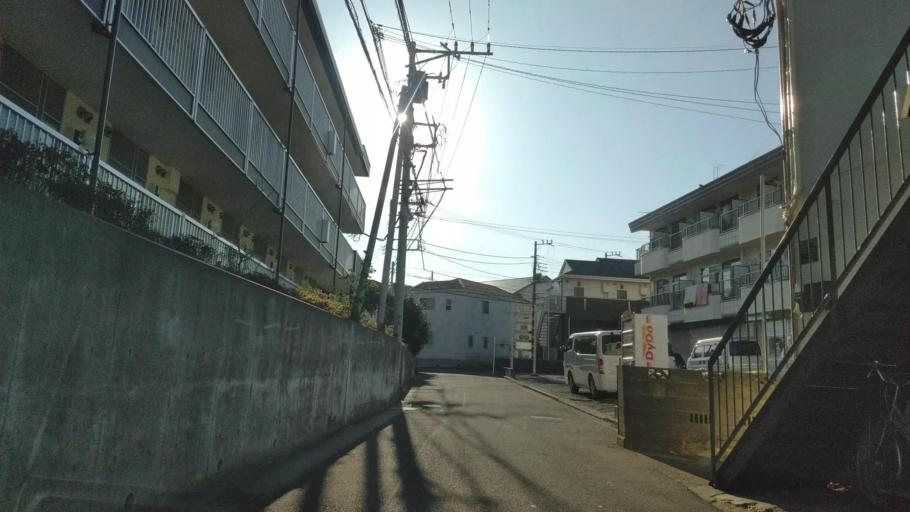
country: JP
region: Kanagawa
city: Hadano
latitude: 35.3622
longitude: 139.2609
